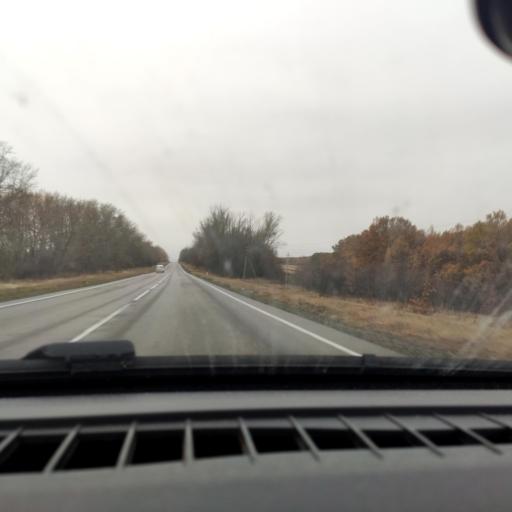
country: RU
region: Voronezj
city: Ostrogozhsk
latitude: 51.0066
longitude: 38.9996
